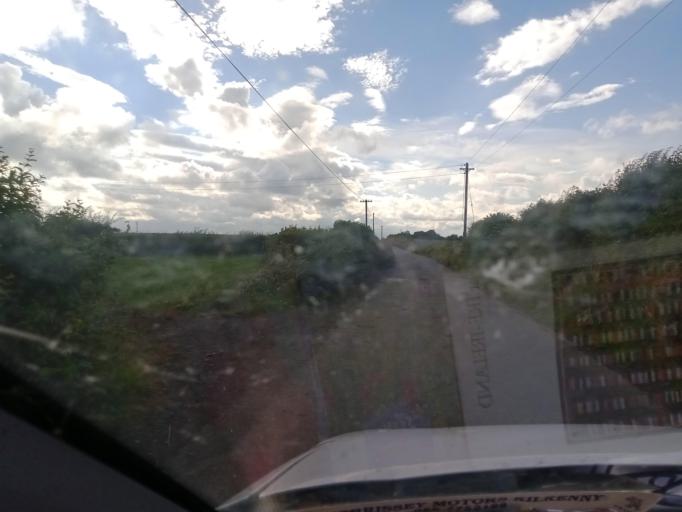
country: IE
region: Leinster
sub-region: Laois
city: Rathdowney
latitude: 52.7755
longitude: -7.5275
